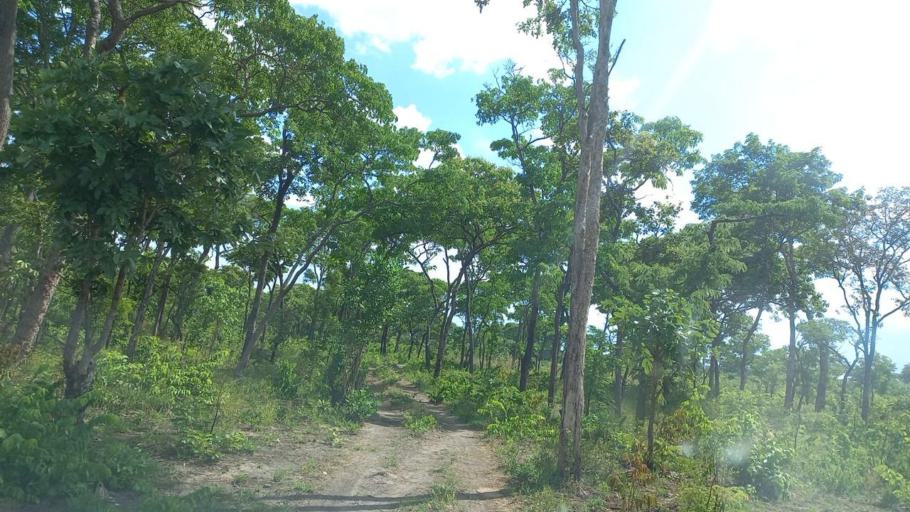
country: ZM
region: North-Western
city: Mufumbwe
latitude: -13.3407
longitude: 24.6315
